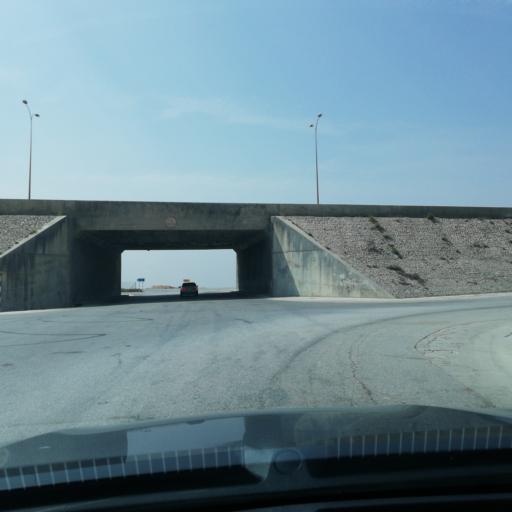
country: OM
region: Zufar
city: Salalah
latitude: 17.2450
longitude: 54.0739
